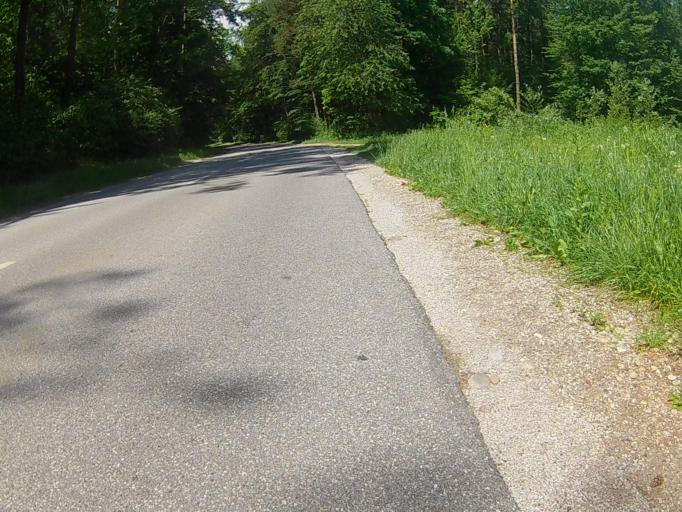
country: SI
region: Miklavz na Dravskem Polju
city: Miklavz na Dravskem Polju
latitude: 46.5023
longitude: 15.6953
